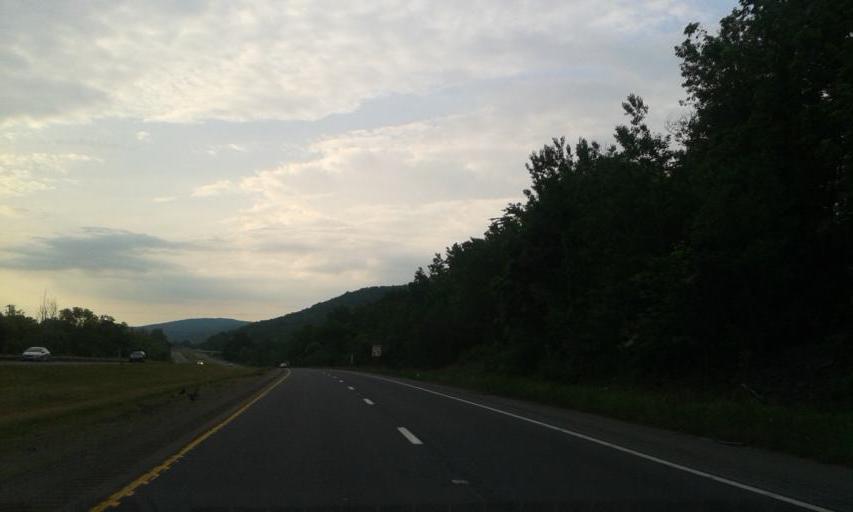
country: US
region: Pennsylvania
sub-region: Susquehanna County
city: Hallstead
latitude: 41.9741
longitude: -75.7409
